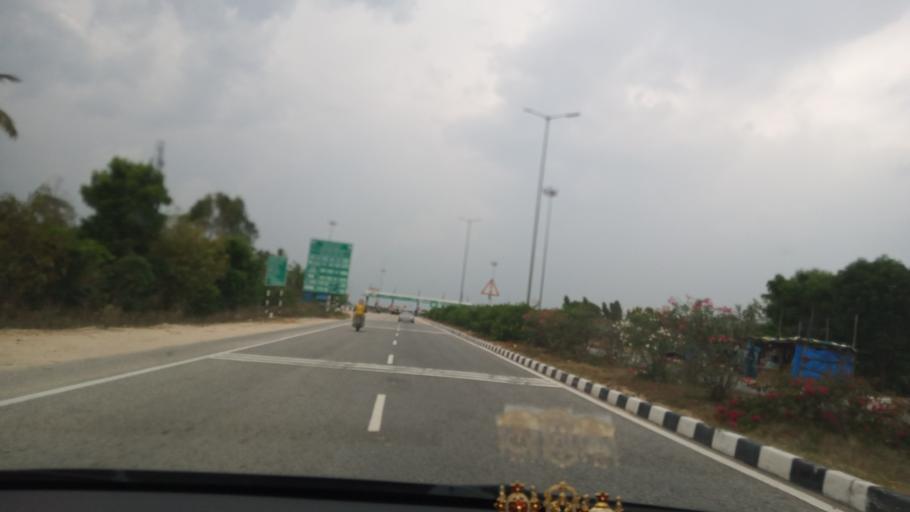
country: IN
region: Karnataka
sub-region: Kolar
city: Mulbagal
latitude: 13.1939
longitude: 78.5477
